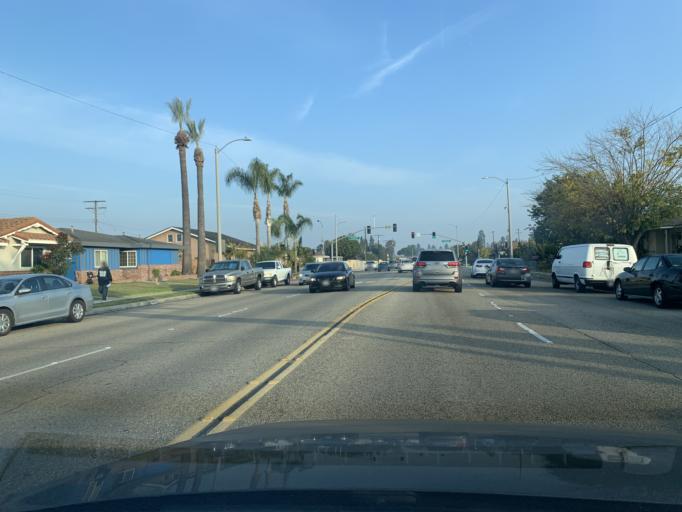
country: US
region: California
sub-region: Orange County
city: Westminster
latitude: 33.7676
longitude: -118.0256
